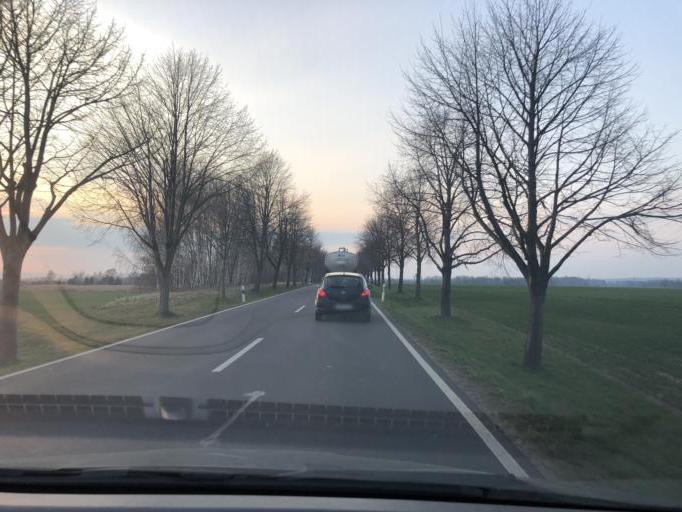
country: DE
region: Saxony
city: Crostwitz
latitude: 51.2151
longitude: 14.2689
